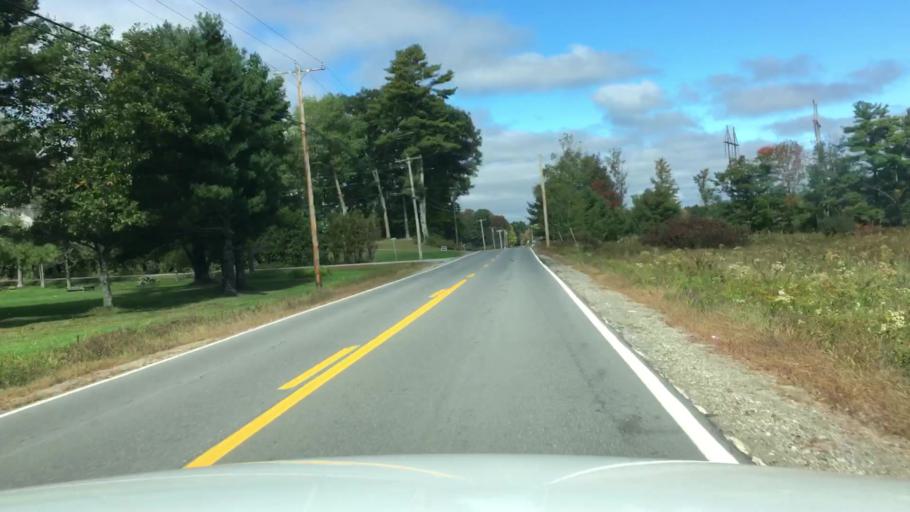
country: US
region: Maine
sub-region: Sagadahoc County
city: North Bath
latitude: 43.9961
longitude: -69.8901
